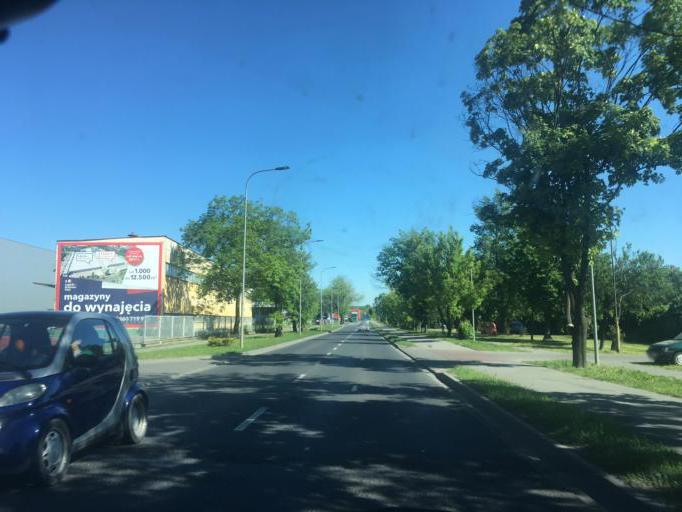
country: PL
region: Kujawsko-Pomorskie
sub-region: Powiat bydgoski
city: Osielsko
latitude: 53.1200
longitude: 18.0874
